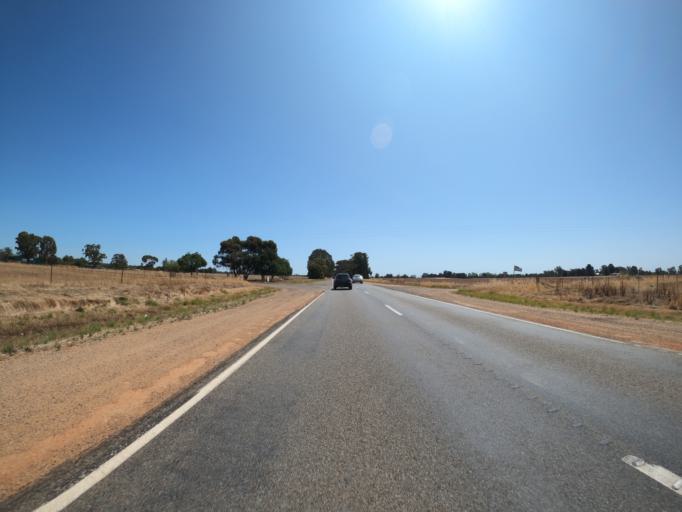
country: AU
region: Victoria
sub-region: Moira
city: Yarrawonga
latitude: -36.0234
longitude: 146.1190
